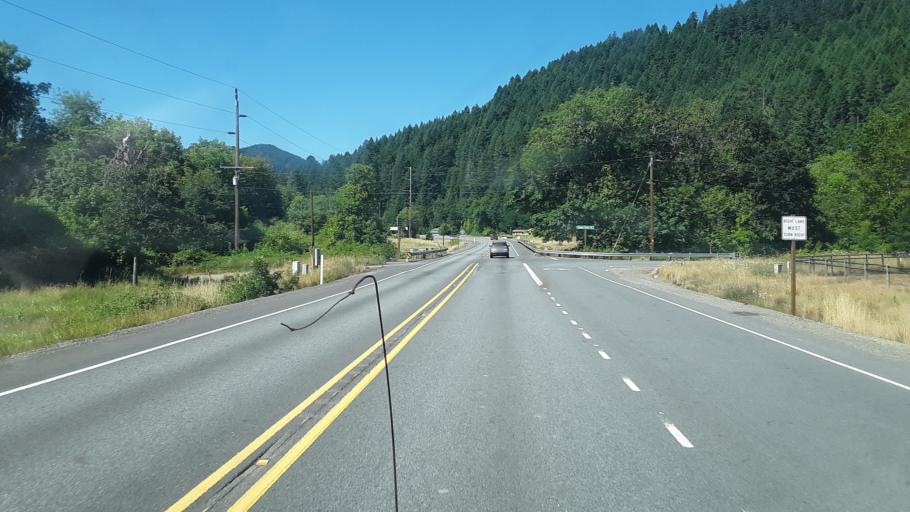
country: US
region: Oregon
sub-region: Josephine County
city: Redwood
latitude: 42.3778
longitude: -123.4950
